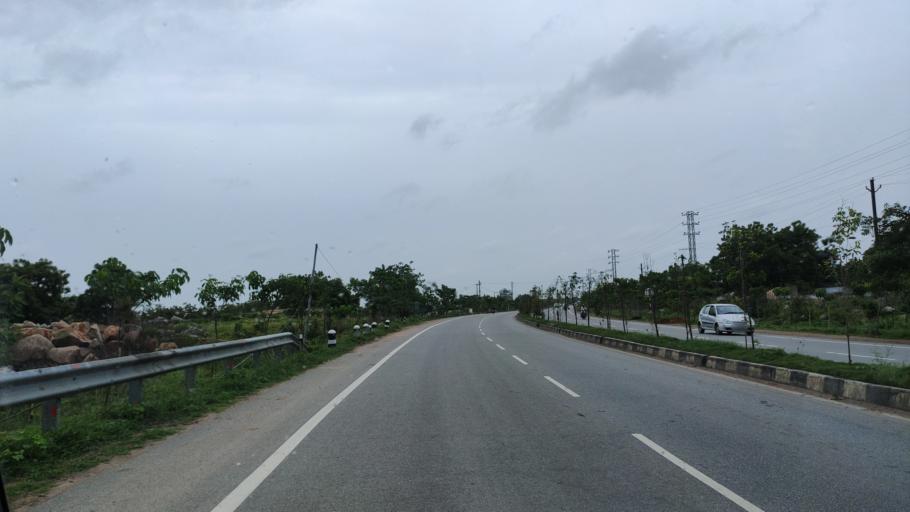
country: IN
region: Telangana
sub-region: Rangareddi
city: Secunderabad
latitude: 17.6026
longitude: 78.5676
